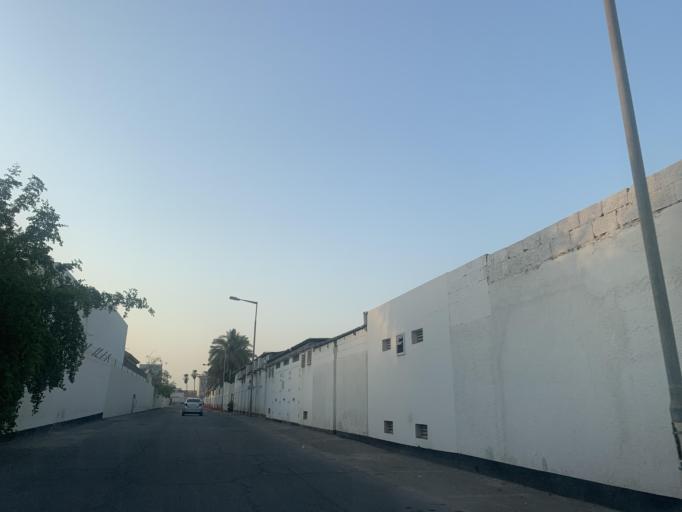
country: BH
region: Manama
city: Jidd Hafs
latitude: 26.2172
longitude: 50.5267
